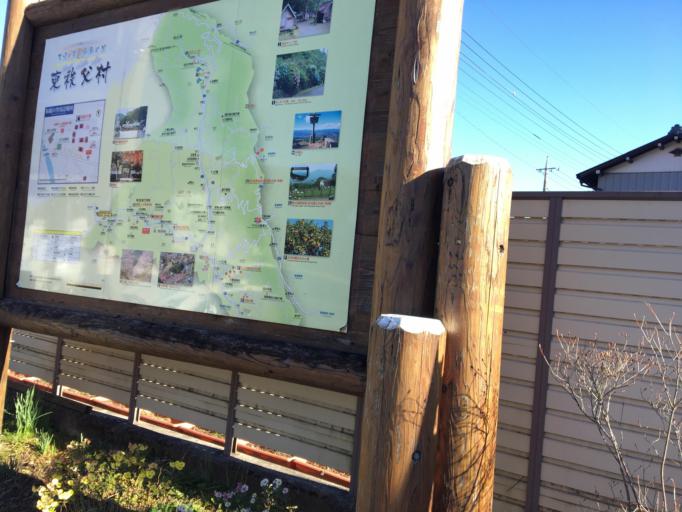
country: JP
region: Saitama
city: Ogawa
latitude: 36.0527
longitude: 139.2037
